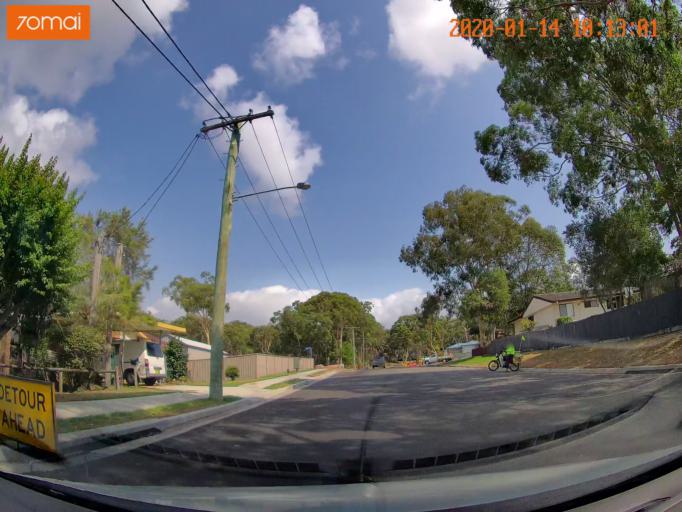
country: AU
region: New South Wales
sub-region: Lake Macquarie Shire
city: Dora Creek
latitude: -33.1139
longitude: 151.5293
